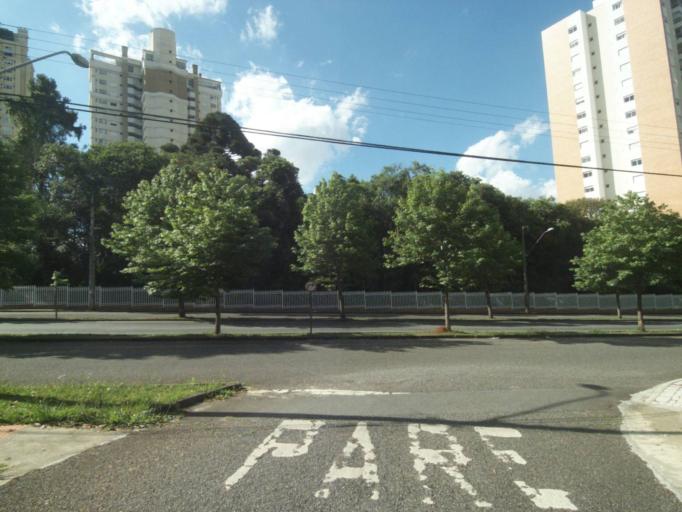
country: BR
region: Parana
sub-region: Curitiba
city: Curitiba
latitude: -25.4385
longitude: -49.3324
